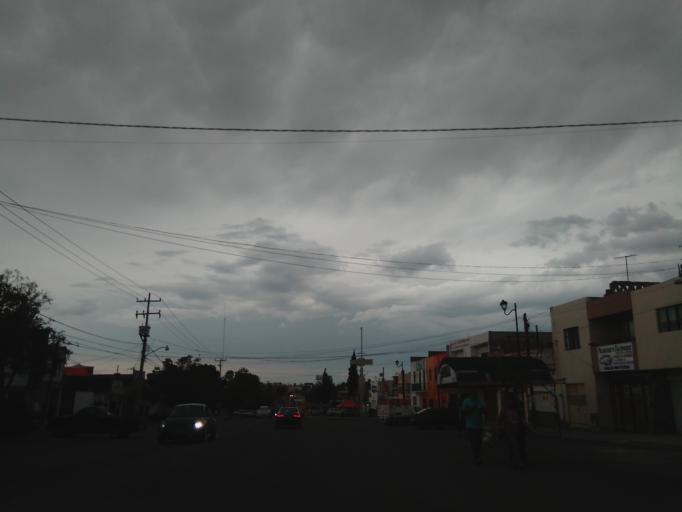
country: MX
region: Guanajuato
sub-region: Dolores Hidalgo Cuna de la Independencia Nacional
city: Dolores Hidalgo Cuna de la Independencia Nacional
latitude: 21.1584
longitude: -100.9265
